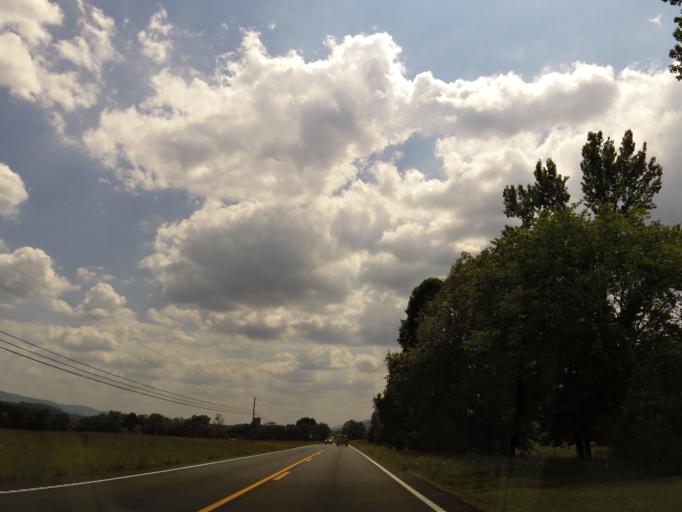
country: US
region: Tennessee
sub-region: Sequatchie County
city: Dunlap
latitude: 35.4535
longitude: -85.3339
